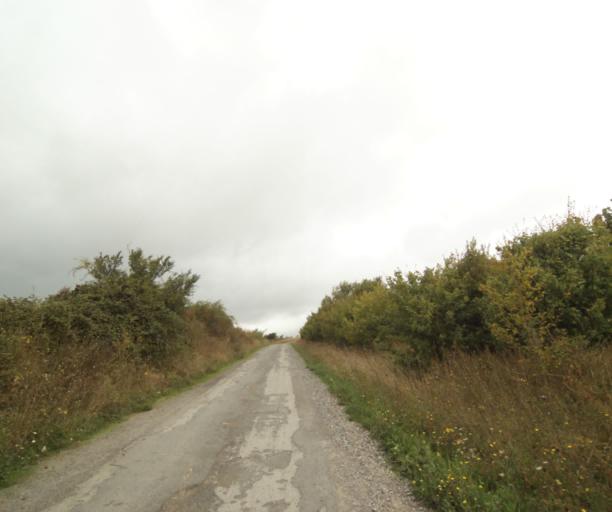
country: FR
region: Nord-Pas-de-Calais
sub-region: Departement du Pas-de-Calais
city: Etaples
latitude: 50.5343
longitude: 1.6804
